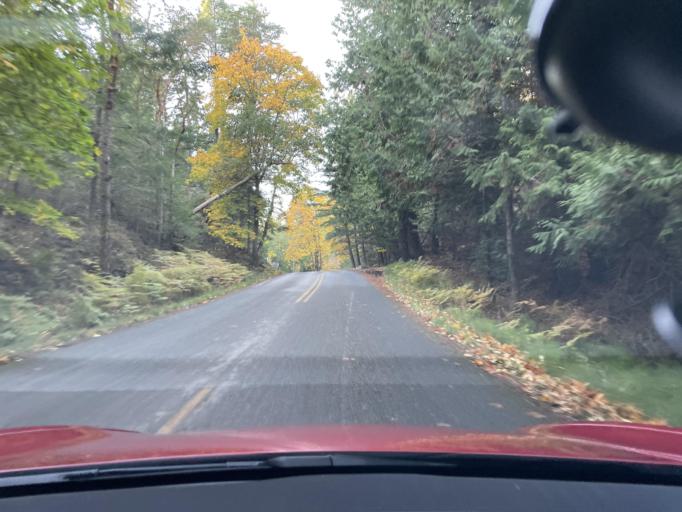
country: US
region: Washington
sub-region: San Juan County
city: Friday Harbor
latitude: 48.5279
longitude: -123.1495
